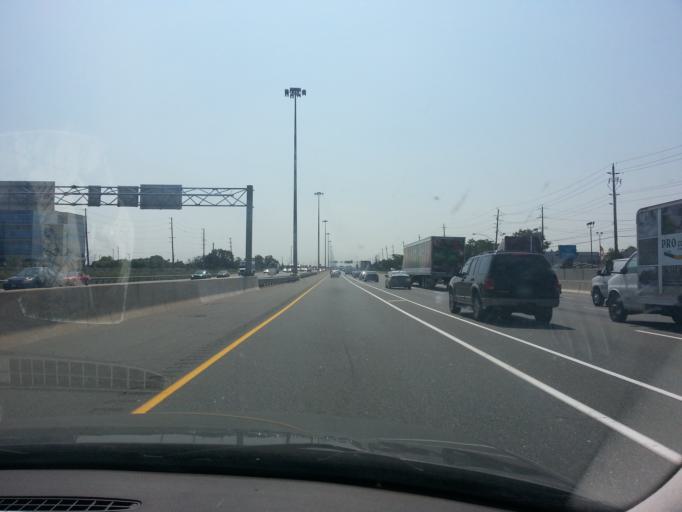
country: CA
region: Ontario
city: Burlington
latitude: 43.3760
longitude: -79.7776
